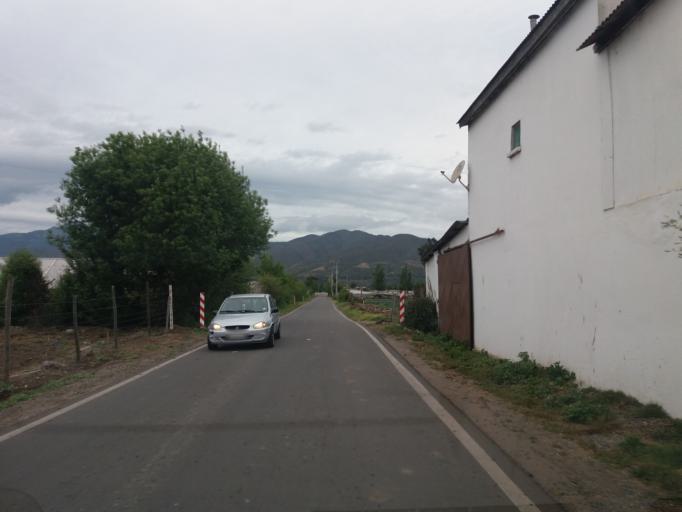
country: CL
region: Valparaiso
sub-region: Provincia de Quillota
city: Quillota
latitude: -32.9187
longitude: -71.2812
